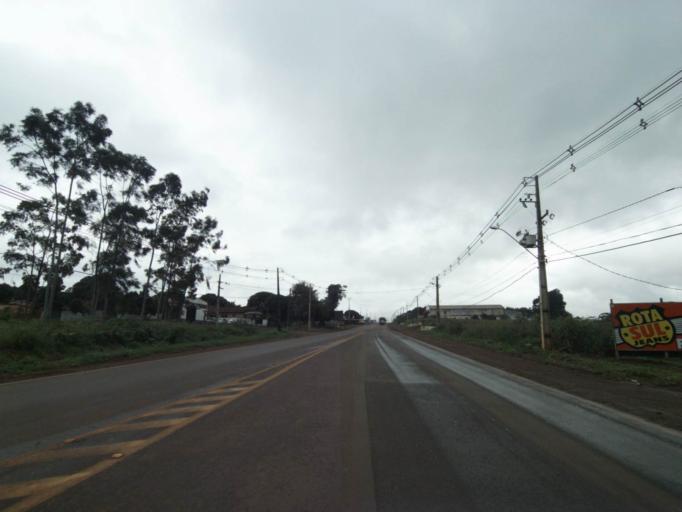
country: BR
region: Parana
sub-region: Marechal Candido Rondon
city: Marechal Candido Rondon
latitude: -24.5684
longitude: -54.0329
